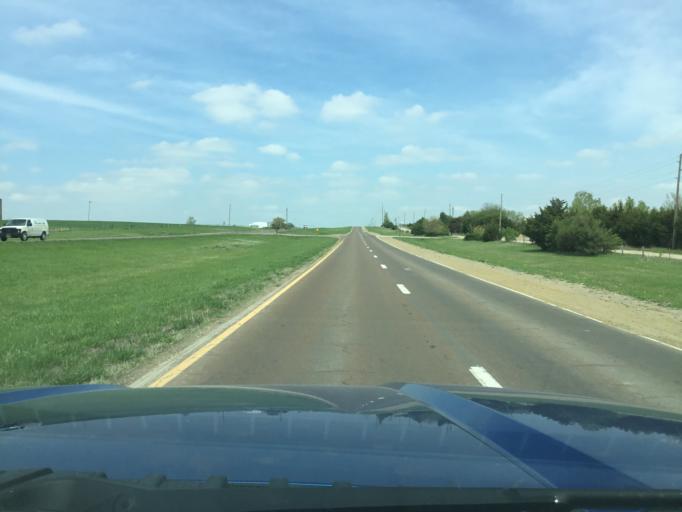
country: US
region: Kansas
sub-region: Osage County
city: Carbondale
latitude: 38.9154
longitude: -95.6874
